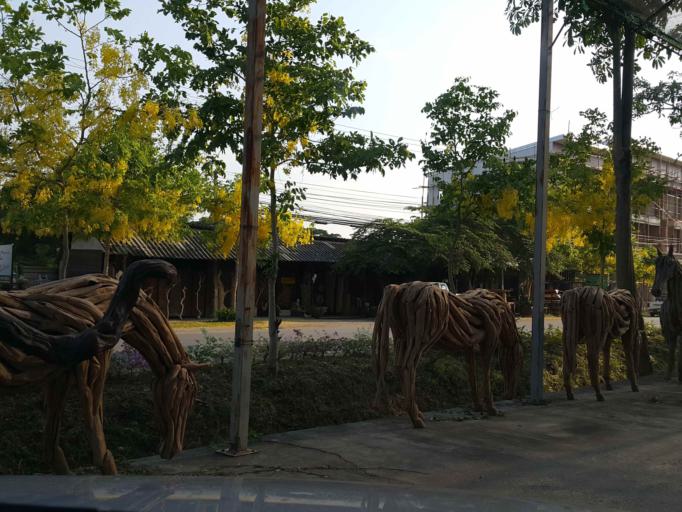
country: TH
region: Chiang Mai
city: Hang Dong
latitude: 18.6894
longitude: 98.9399
